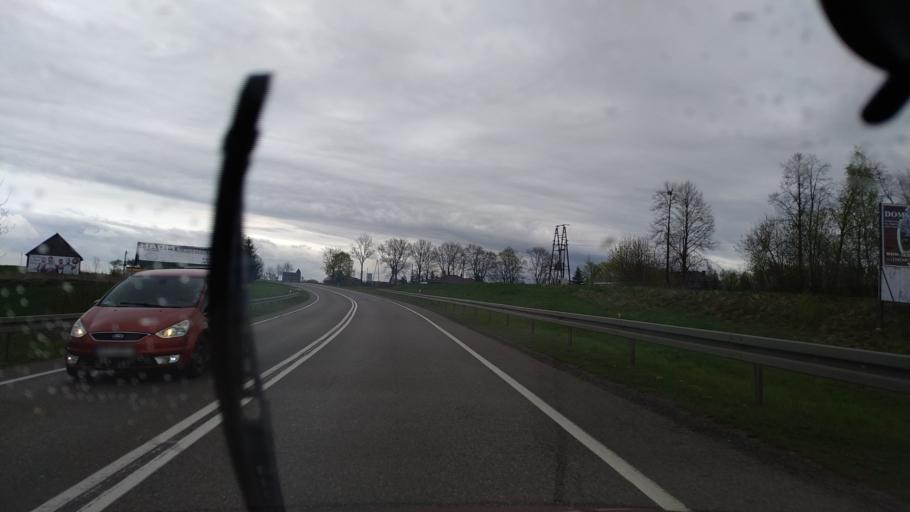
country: PL
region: Pomeranian Voivodeship
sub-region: Powiat starogardzki
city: Lubichowo
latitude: 53.9322
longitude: 18.4094
